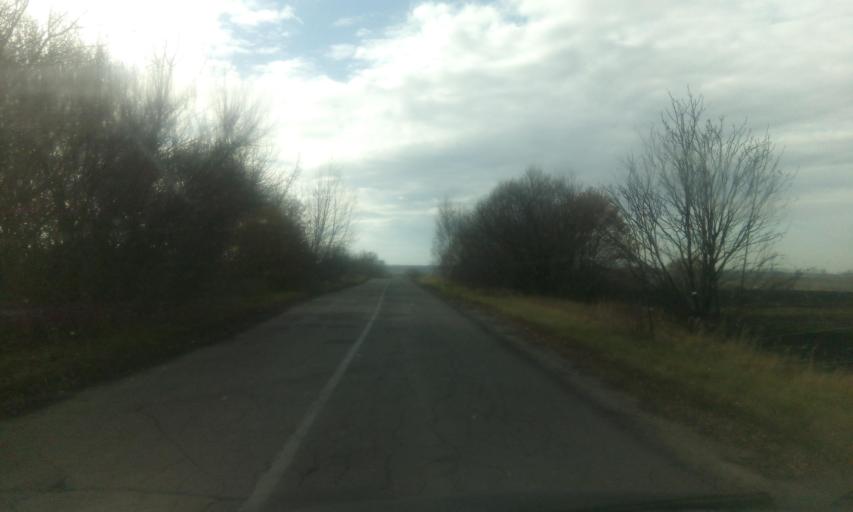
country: RU
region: Tula
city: Dubovka
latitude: 53.9546
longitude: 38.0344
